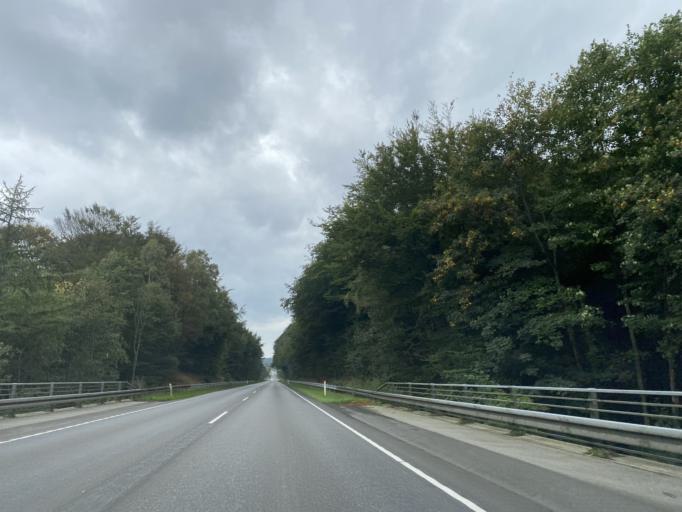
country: DK
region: Central Jutland
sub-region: Viborg Kommune
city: Bjerringbro
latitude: 56.3220
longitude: 9.5662
